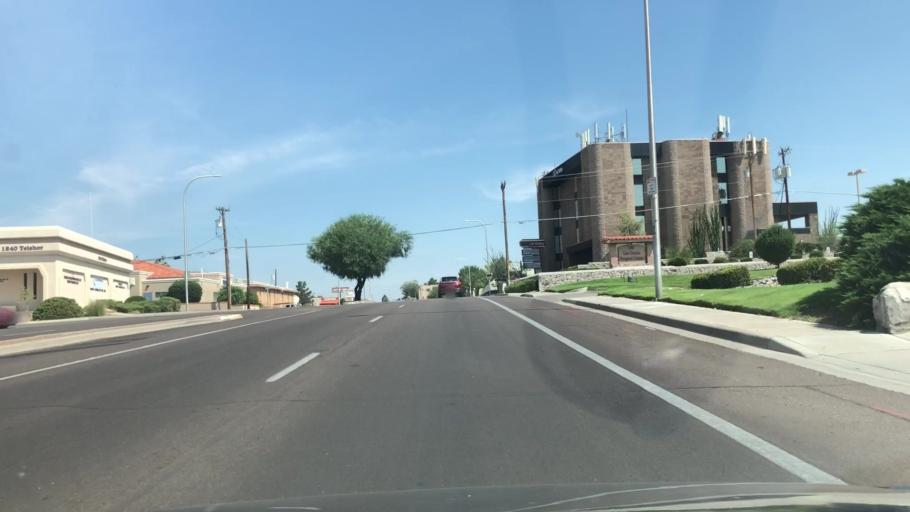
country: US
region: New Mexico
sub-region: Dona Ana County
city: University Park
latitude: 32.3048
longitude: -106.7381
